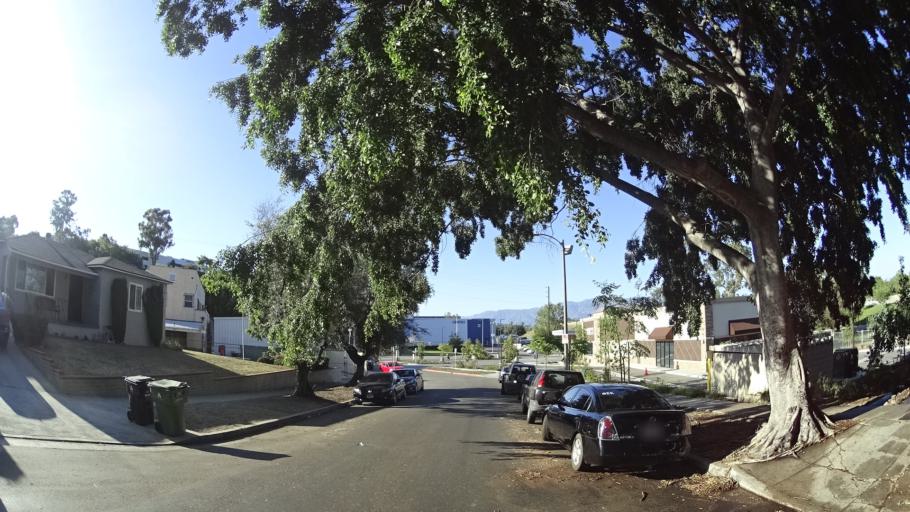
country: US
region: California
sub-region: Los Angeles County
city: Belvedere
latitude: 34.0735
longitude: -118.1622
